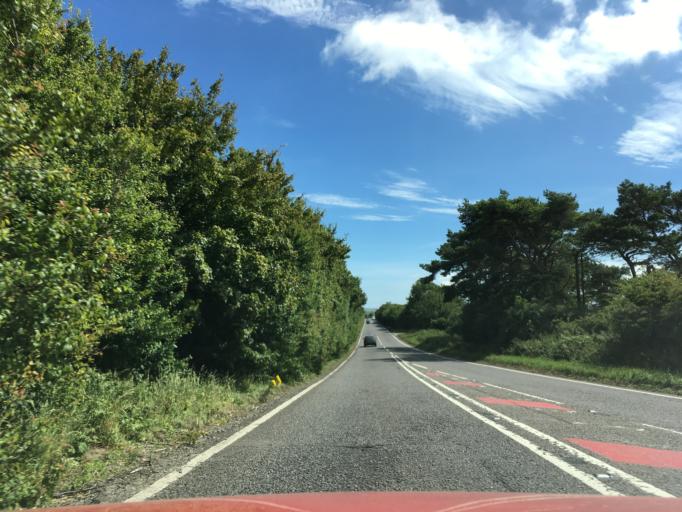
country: GB
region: England
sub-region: Dorset
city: Dorchester
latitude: 50.7777
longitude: -2.5394
